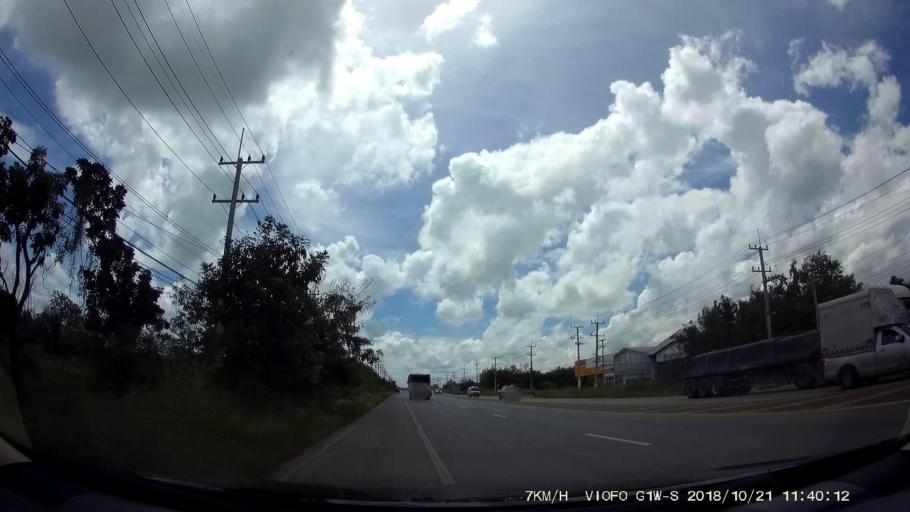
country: TH
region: Chaiyaphum
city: Chaiyaphum
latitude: 15.7152
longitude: 102.0159
